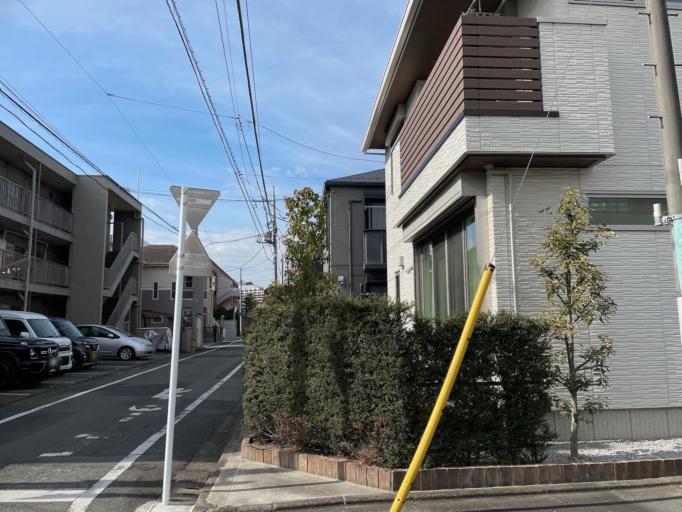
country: JP
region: Tokyo
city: Hino
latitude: 35.6946
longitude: 139.4313
